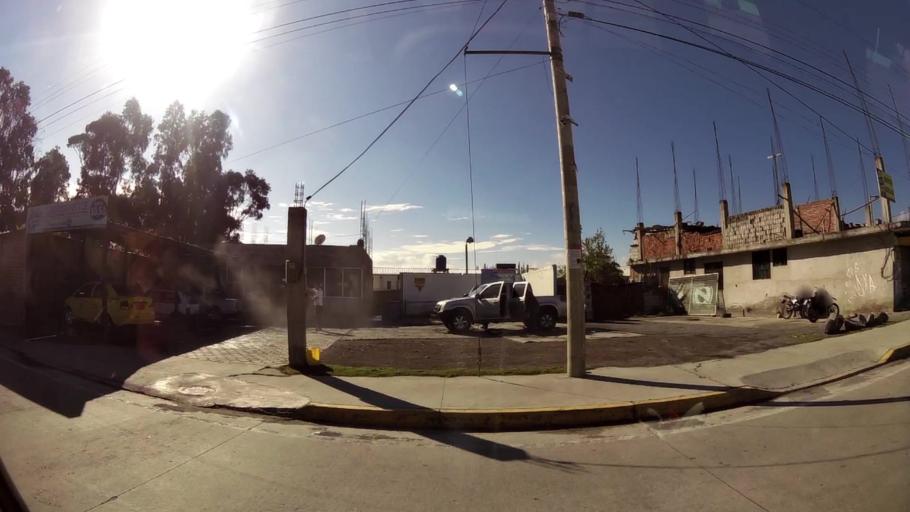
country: EC
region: Chimborazo
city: Riobamba
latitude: -1.6480
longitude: -78.6883
